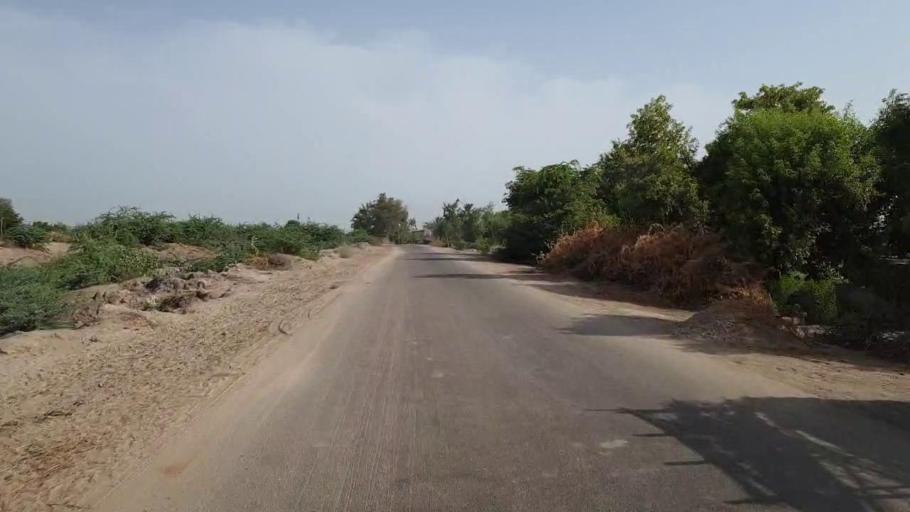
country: PK
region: Sindh
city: Sakrand
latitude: 26.2642
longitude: 68.2813
